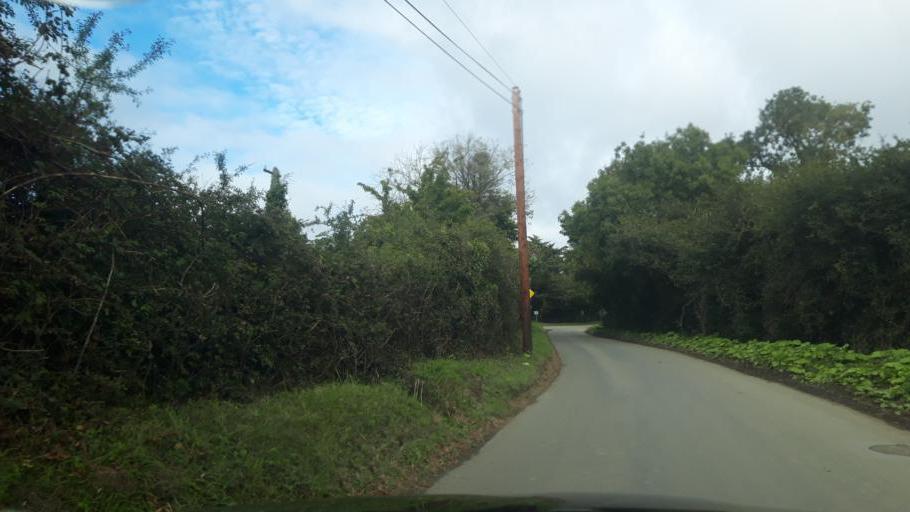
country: IE
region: Leinster
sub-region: Fingal County
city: Swords
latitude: 53.4906
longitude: -6.2847
